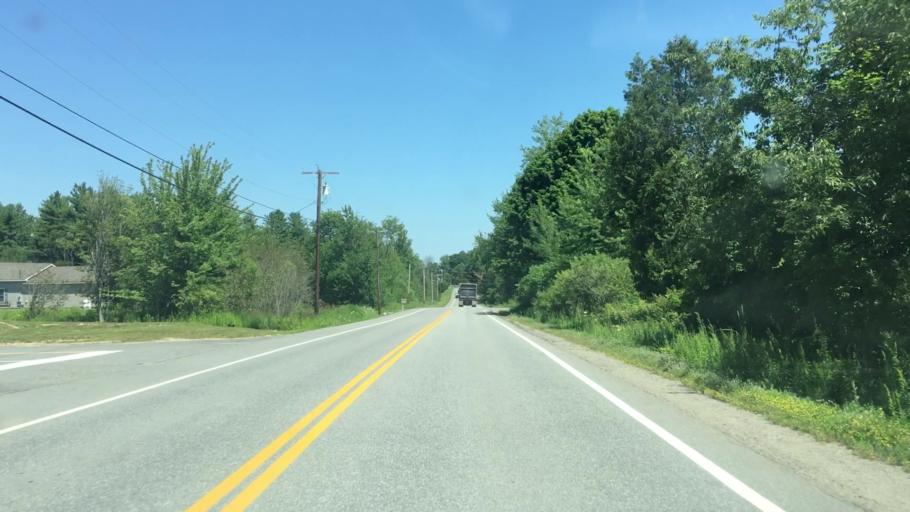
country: US
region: Maine
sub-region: Penobscot County
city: Bangor
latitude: 44.8301
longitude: -68.8135
